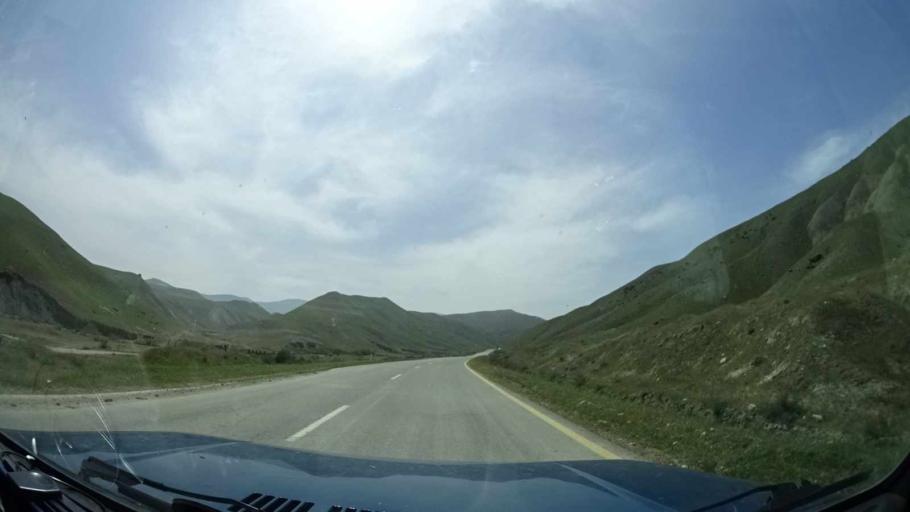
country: AZ
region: Xizi
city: Kilyazi
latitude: 40.8512
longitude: 49.2693
